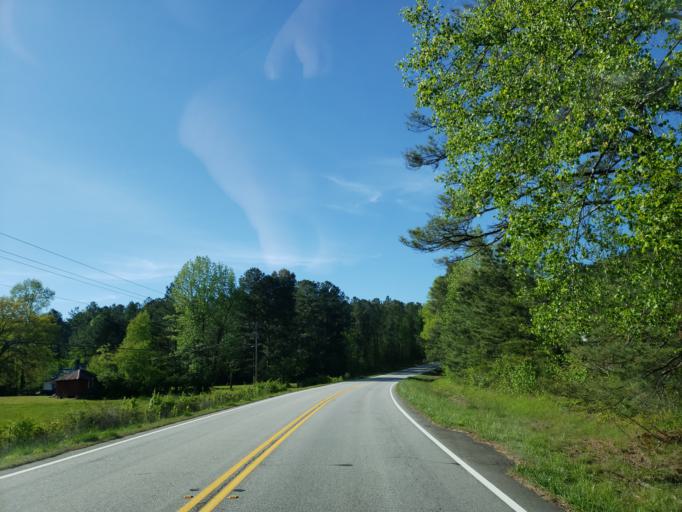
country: US
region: Georgia
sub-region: Haralson County
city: Tallapoosa
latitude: 33.8801
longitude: -85.3102
